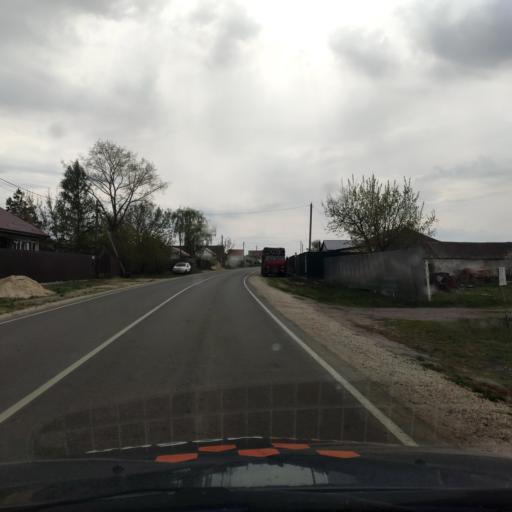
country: RU
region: Voronezj
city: Podgornoye
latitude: 51.8519
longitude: 39.1499
